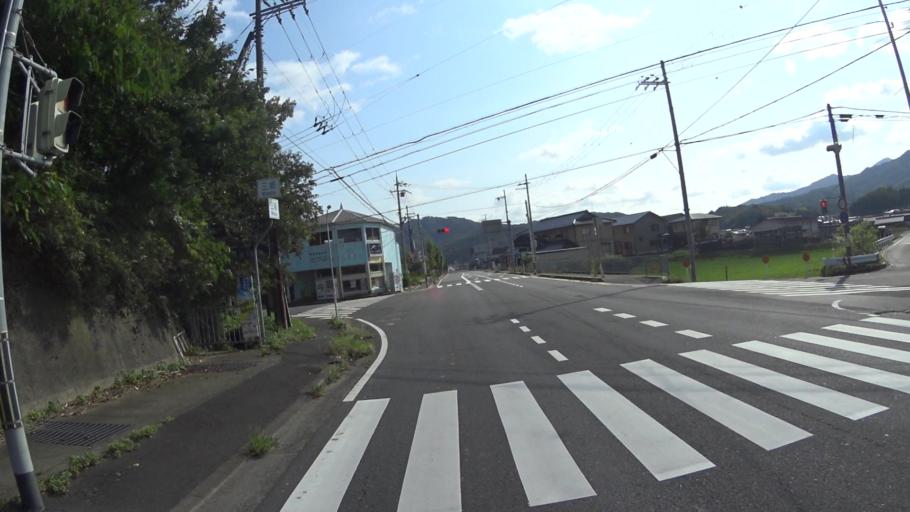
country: JP
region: Kyoto
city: Miyazu
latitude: 35.5788
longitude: 135.0994
